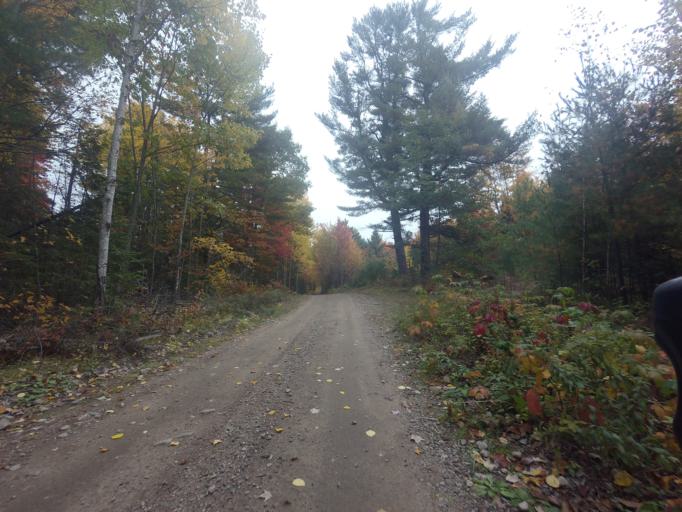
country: CA
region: Ontario
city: Petawawa
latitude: 45.7509
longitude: -77.2729
